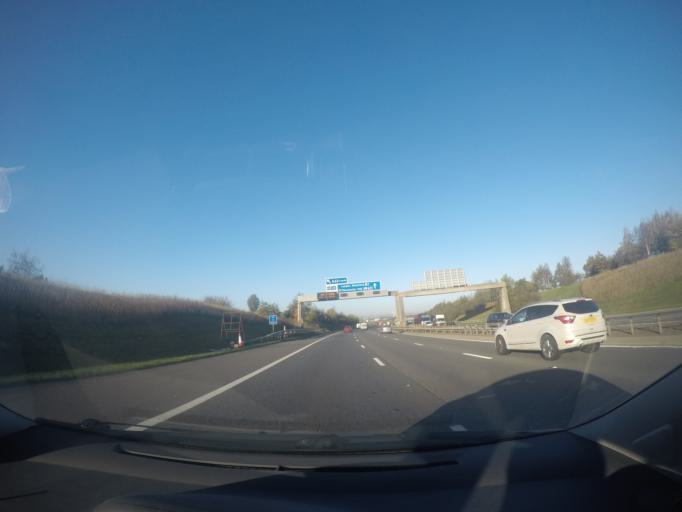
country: GB
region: England
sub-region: City and Borough of Leeds
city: Swillington
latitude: 53.7740
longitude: -1.4450
